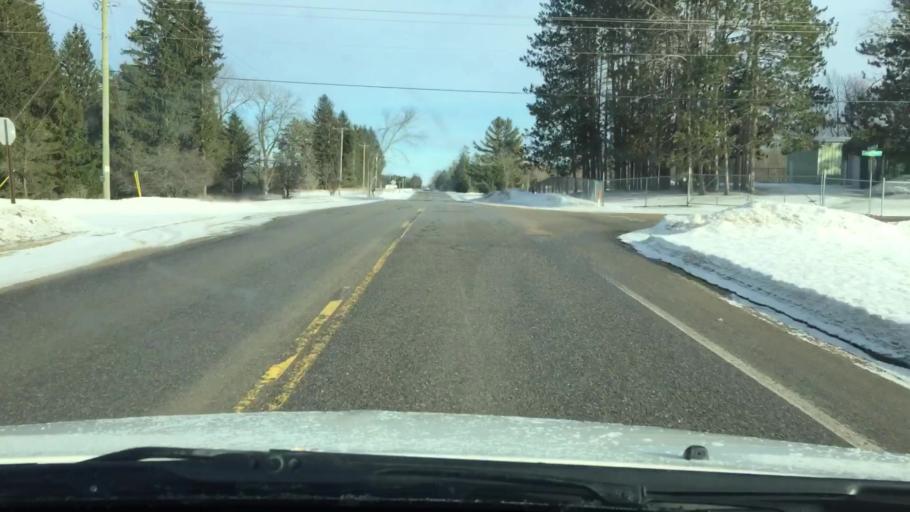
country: US
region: Michigan
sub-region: Kalkaska County
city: Kalkaska
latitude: 44.6408
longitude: -85.2513
